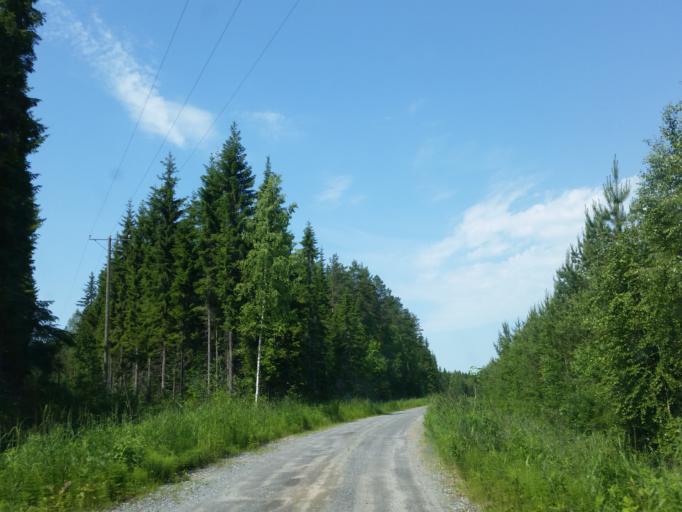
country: FI
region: Northern Savo
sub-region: Ylae-Savo
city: Keitele
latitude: 63.1012
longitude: 26.5476
